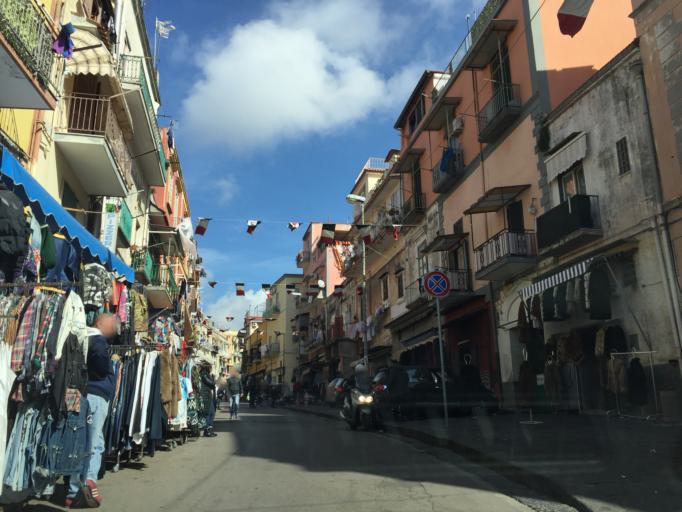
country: IT
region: Campania
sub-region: Provincia di Napoli
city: Ercolano
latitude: 40.8103
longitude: 14.3504
